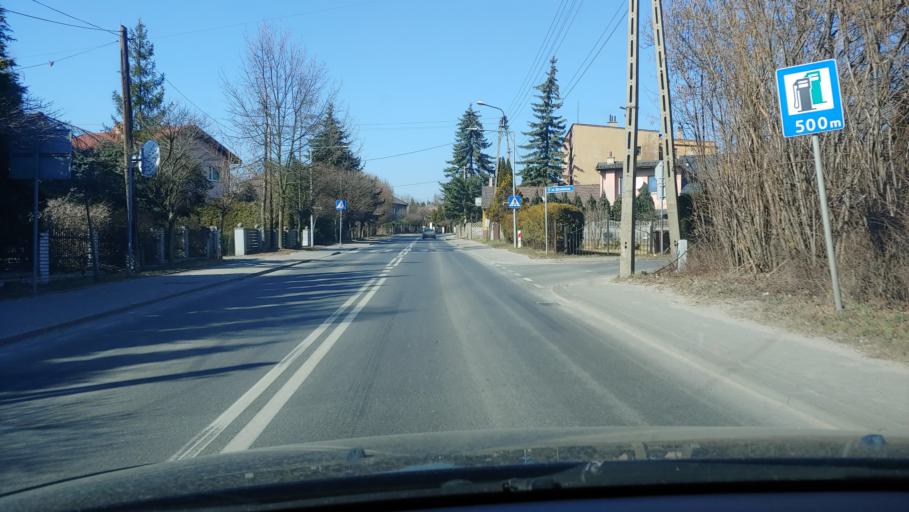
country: PL
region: Lesser Poland Voivodeship
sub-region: Powiat chrzanowski
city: Trzebinia
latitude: 50.1672
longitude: 19.4731
